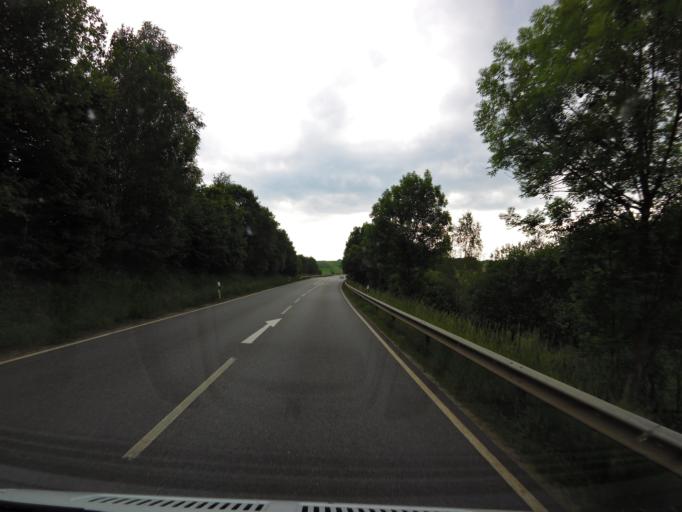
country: DE
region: Bavaria
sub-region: Lower Bavaria
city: Neukirchen vorm Wald
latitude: 48.6838
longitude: 13.3682
